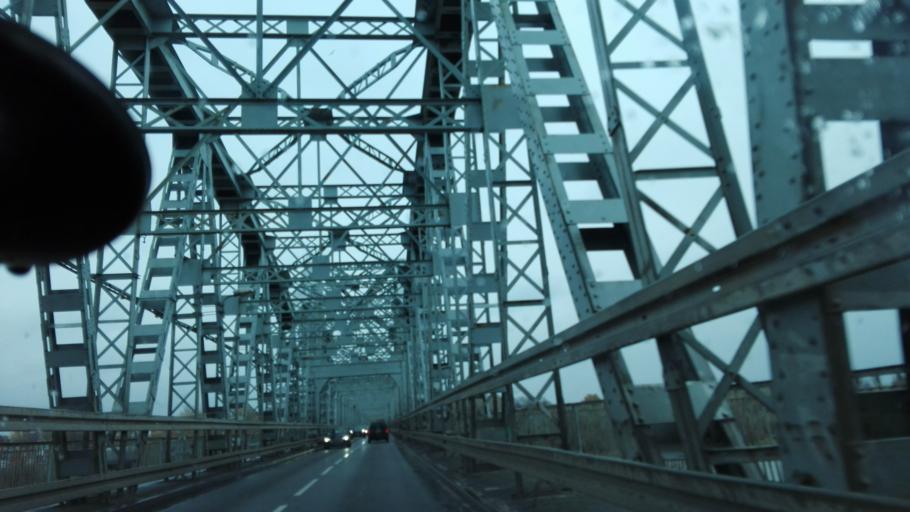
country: PL
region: Lublin Voivodeship
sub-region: Powiat pulawski
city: Pulawy
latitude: 51.4137
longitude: 21.9439
